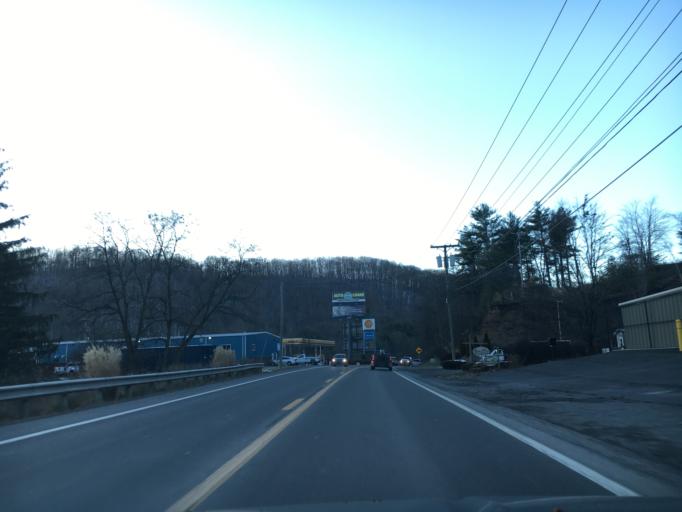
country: US
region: West Virginia
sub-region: Raleigh County
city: Daniels
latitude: 37.7295
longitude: -81.1104
